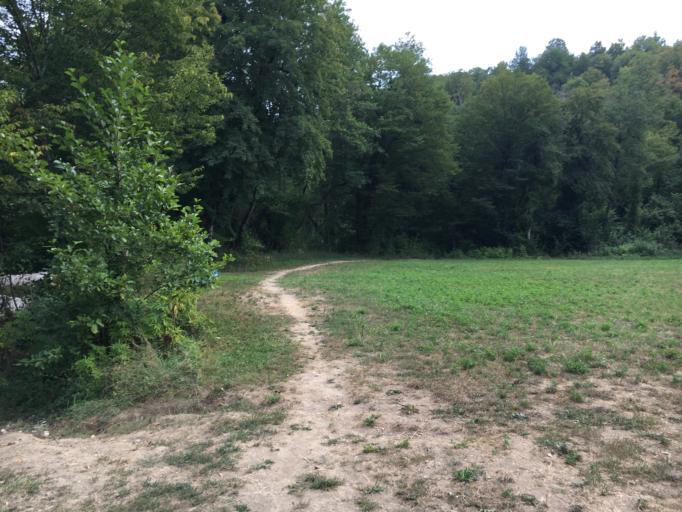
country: RU
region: Krasnodarskiy
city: Tuapse
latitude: 44.2577
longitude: 39.2194
